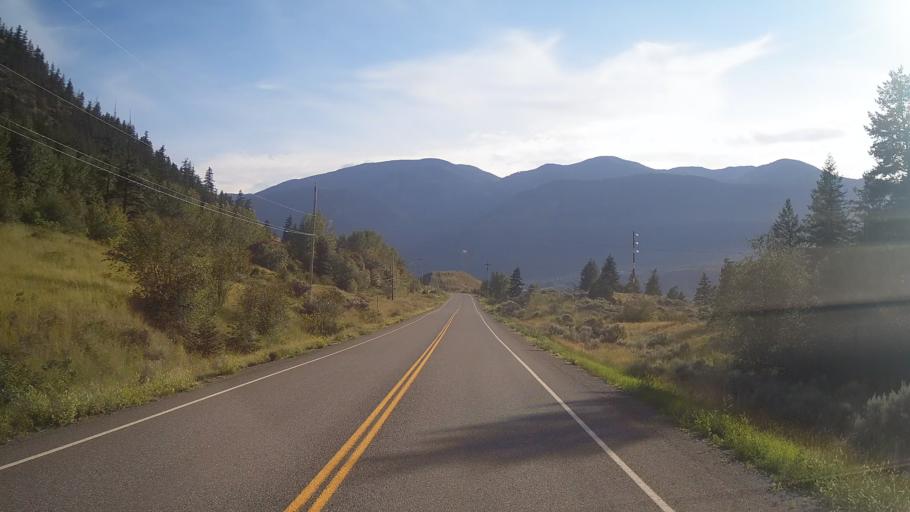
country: CA
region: British Columbia
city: Lillooet
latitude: 50.8673
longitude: -121.8459
